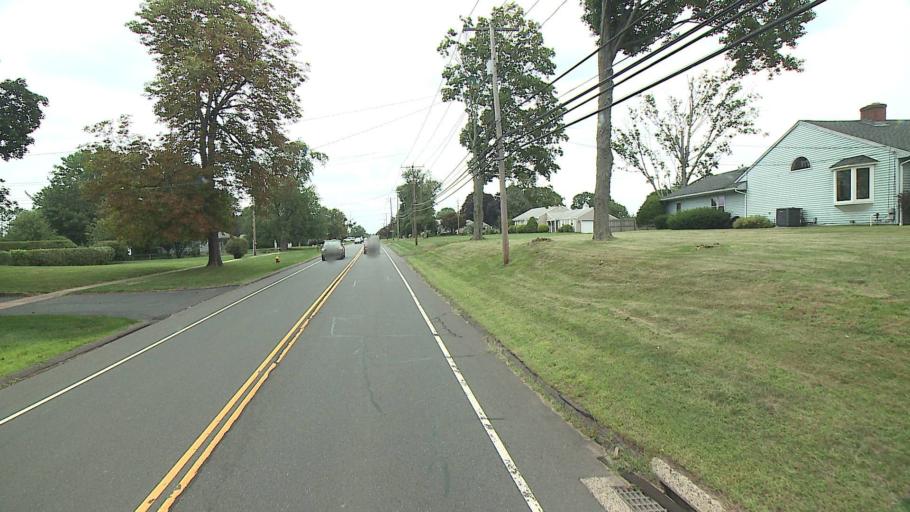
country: US
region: Connecticut
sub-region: Hartford County
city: Wethersfield
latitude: 41.6747
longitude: -72.6665
